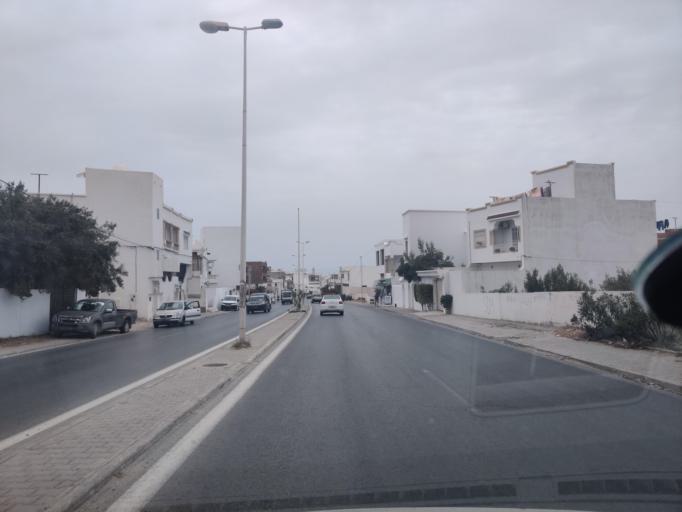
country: TN
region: Nabul
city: Al Hammamat
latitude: 36.4092
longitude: 10.6227
